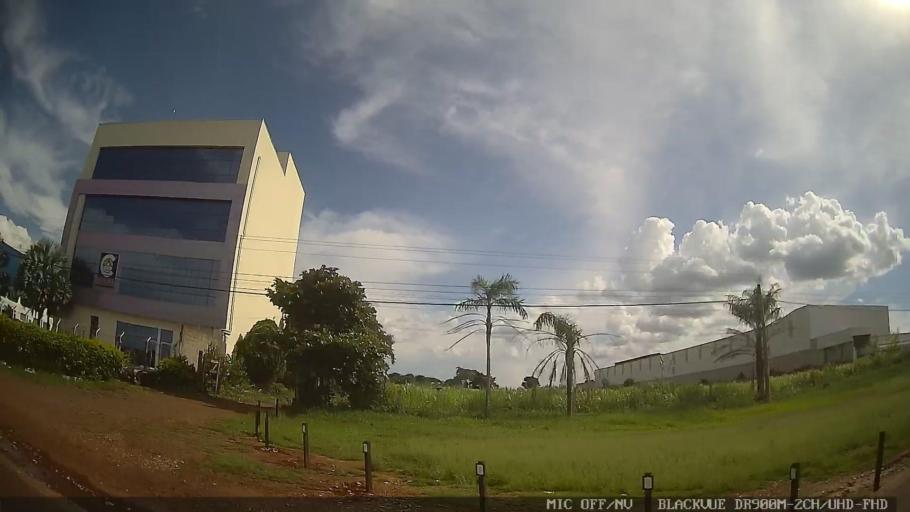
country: BR
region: Sao Paulo
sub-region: Laranjal Paulista
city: Laranjal Paulista
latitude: -23.0373
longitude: -47.8702
